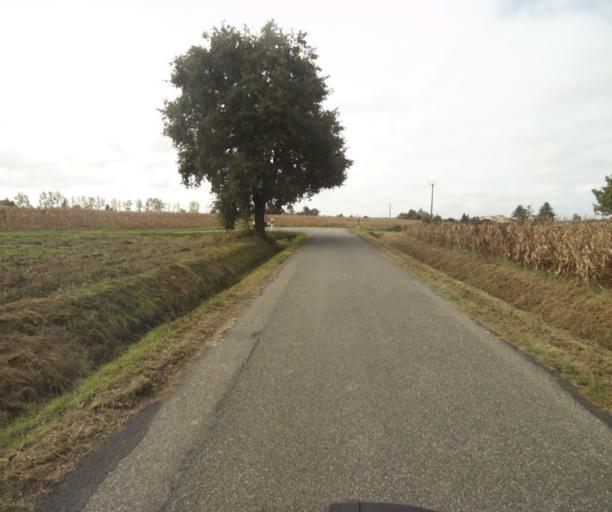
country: FR
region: Midi-Pyrenees
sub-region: Departement du Tarn-et-Garonne
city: Finhan
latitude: 43.9180
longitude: 1.2410
